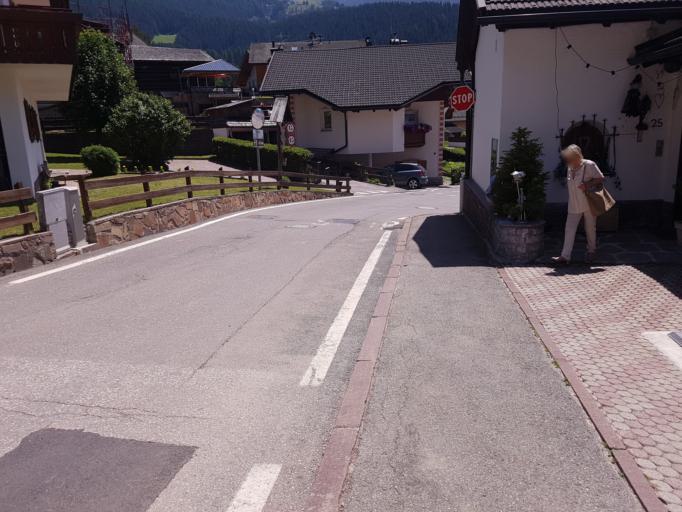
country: IT
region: Trentino-Alto Adige
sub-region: Bolzano
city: Santa Cristina Valgardena
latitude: 46.5618
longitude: 11.7356
